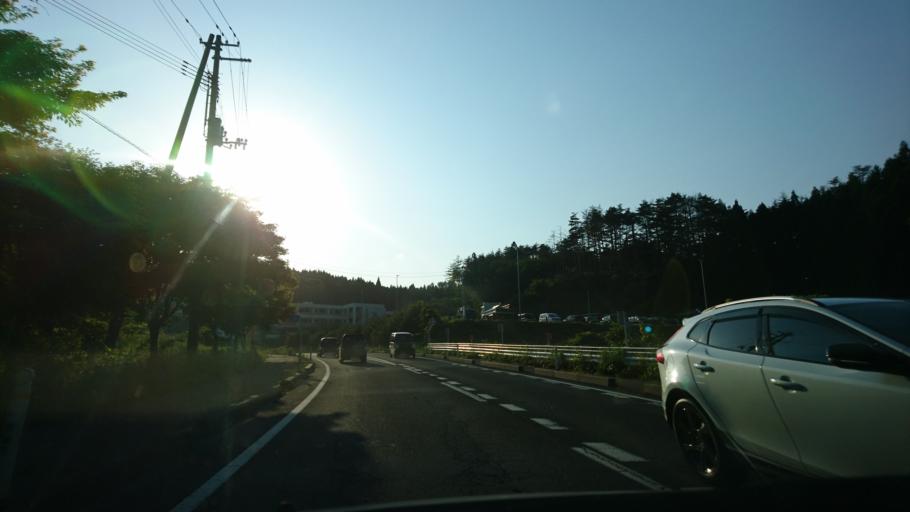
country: JP
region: Iwate
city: Ofunato
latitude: 38.9157
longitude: 141.5224
